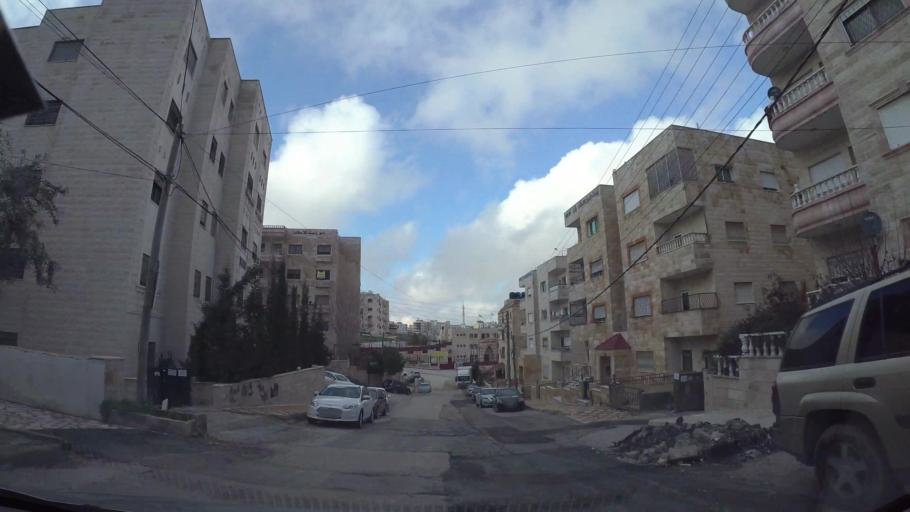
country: JO
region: Amman
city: Al Jubayhah
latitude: 32.0501
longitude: 35.8900
